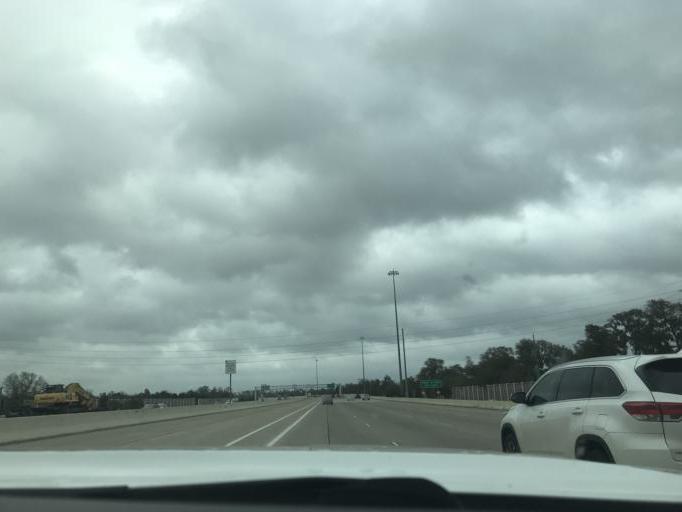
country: US
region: Texas
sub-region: Fort Bend County
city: Greatwood
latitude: 29.5634
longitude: -95.6801
